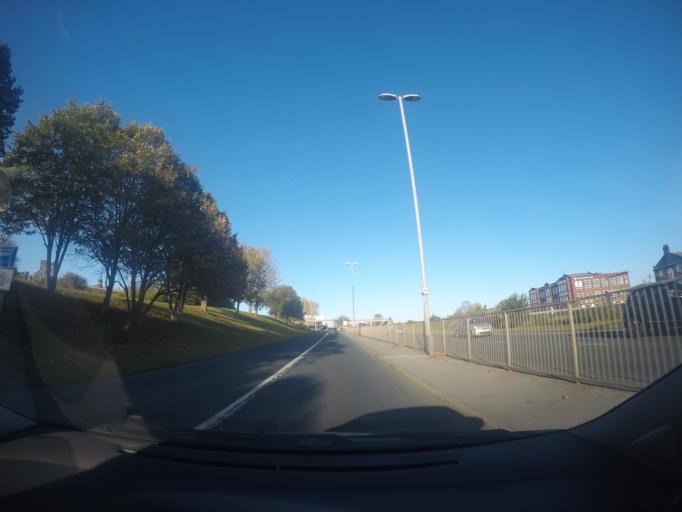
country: GB
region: England
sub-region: City and Borough of Leeds
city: Leeds
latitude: 53.7966
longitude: -1.5722
